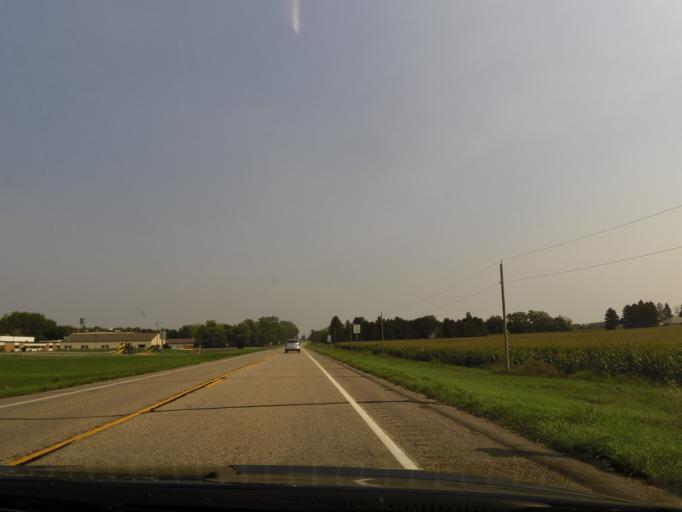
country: US
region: Minnesota
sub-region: Traverse County
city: Wheaton
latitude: 45.8634
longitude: -96.7399
